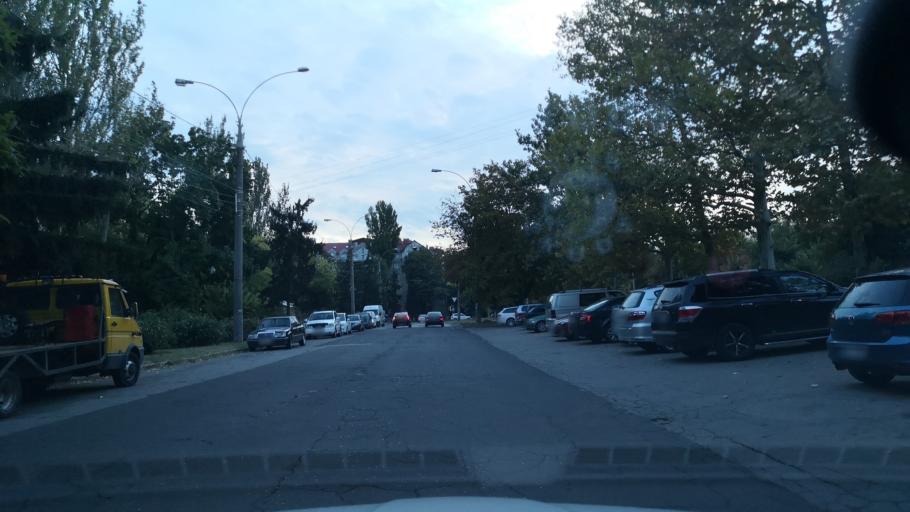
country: MD
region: Chisinau
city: Chisinau
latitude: 46.9854
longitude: 28.8482
